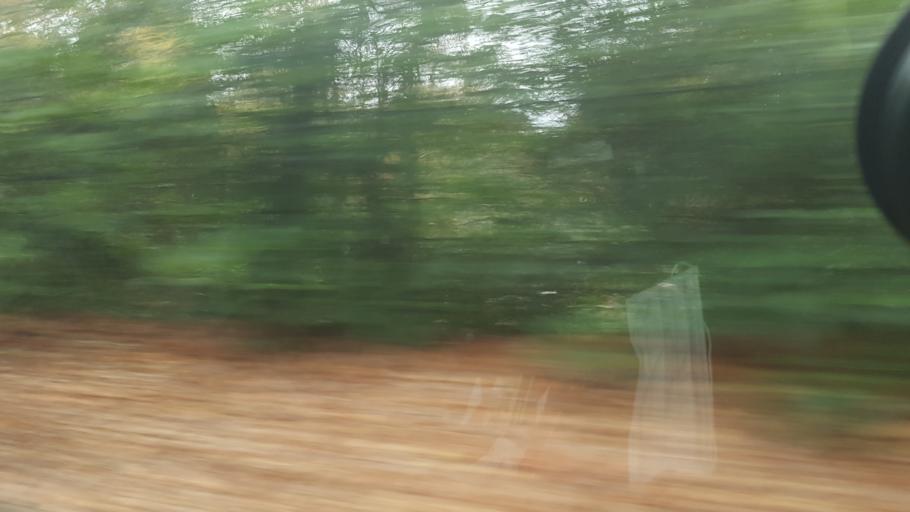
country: GB
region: England
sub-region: Bracknell Forest
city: Sandhurst
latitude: 51.3179
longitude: -0.7794
